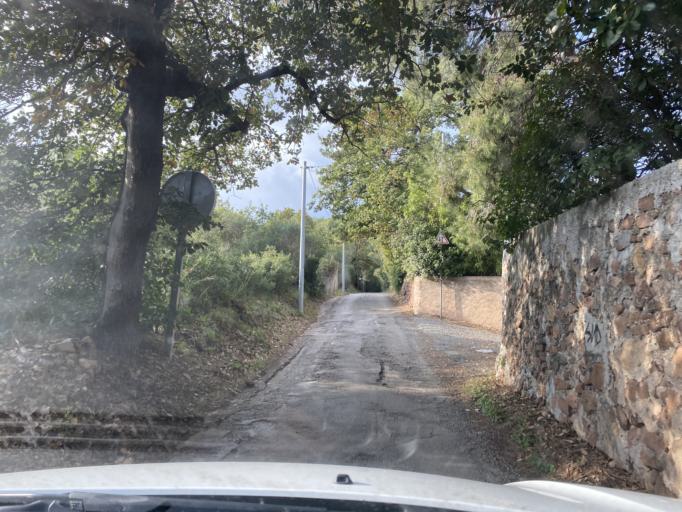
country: FR
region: Provence-Alpes-Cote d'Azur
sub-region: Departement du Var
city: La Seyne-sur-Mer
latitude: 43.1210
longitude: 5.8742
